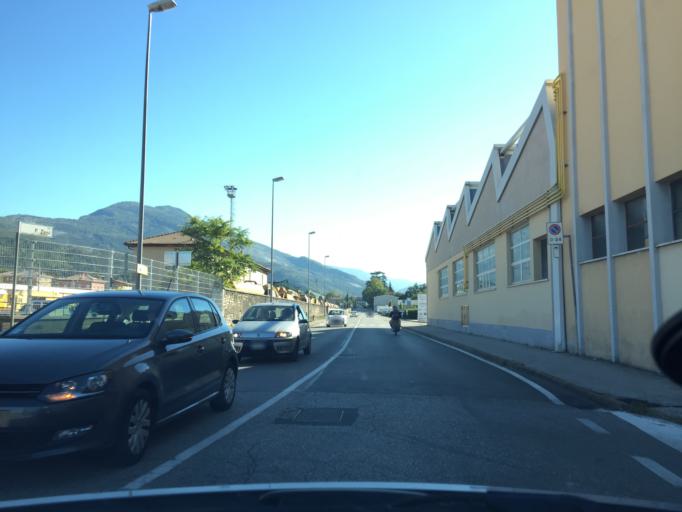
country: IT
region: Trentino-Alto Adige
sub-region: Provincia di Trento
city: Rovereto
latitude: 45.8919
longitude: 11.0328
